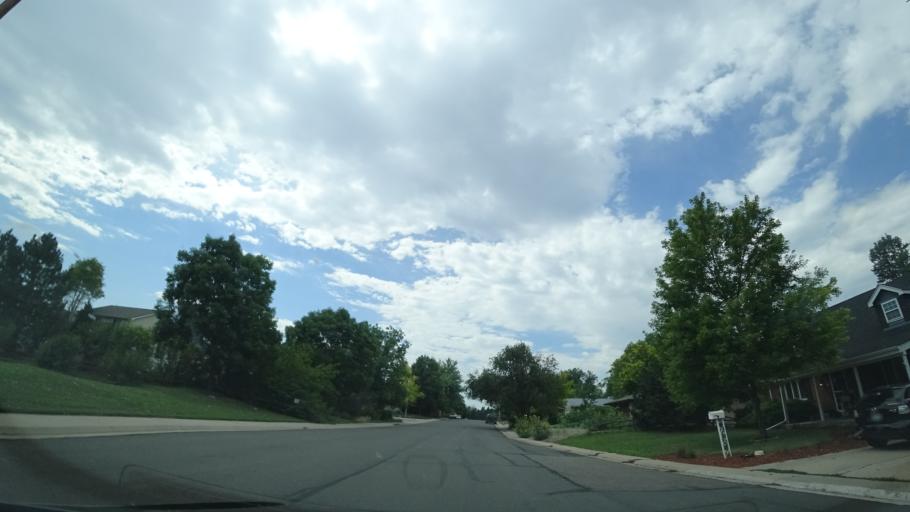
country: US
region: Colorado
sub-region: Jefferson County
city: Lakewood
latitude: 39.7223
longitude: -105.0723
